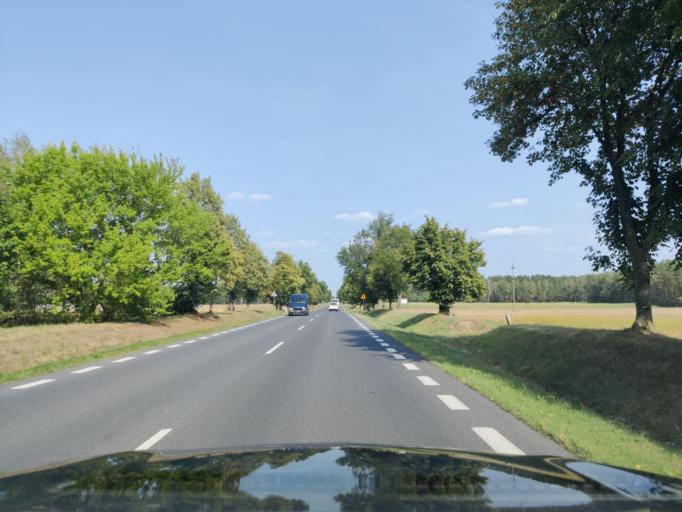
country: PL
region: Masovian Voivodeship
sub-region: Powiat makowski
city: Szelkow
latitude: 52.8348
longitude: 21.2421
